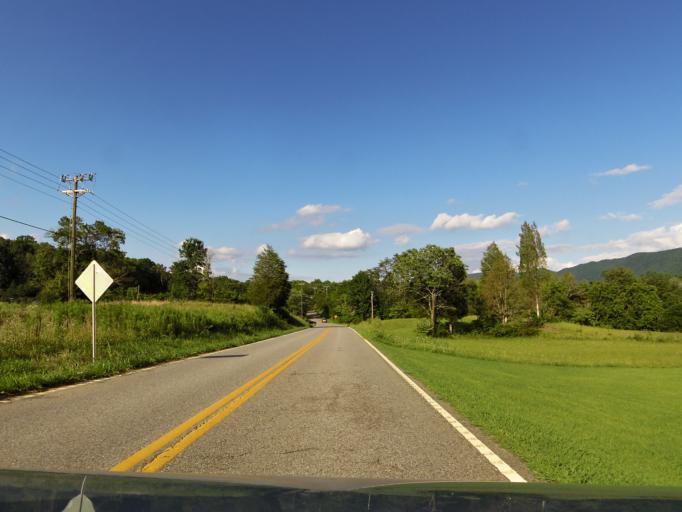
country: US
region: Tennessee
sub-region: Blount County
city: Maryville
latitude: 35.6330
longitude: -84.0114
